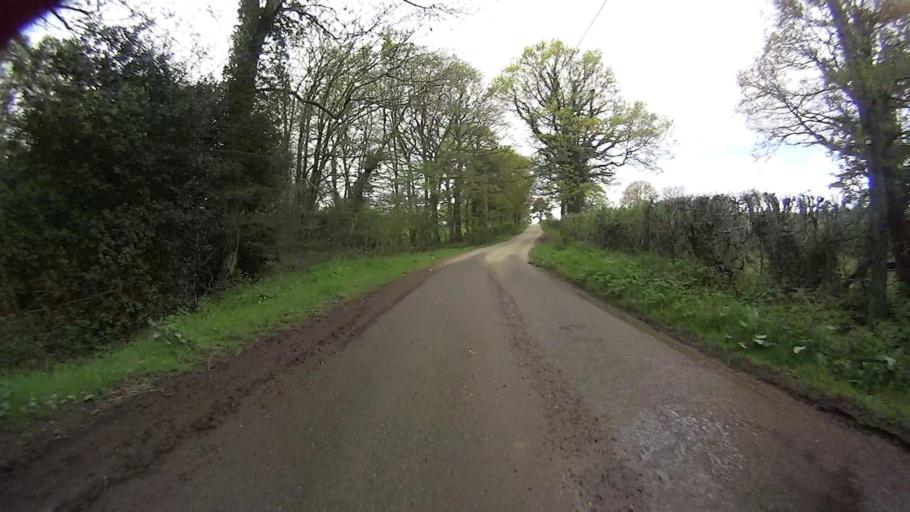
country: GB
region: England
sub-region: West Sussex
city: Horsham
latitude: 51.1104
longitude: -0.3109
